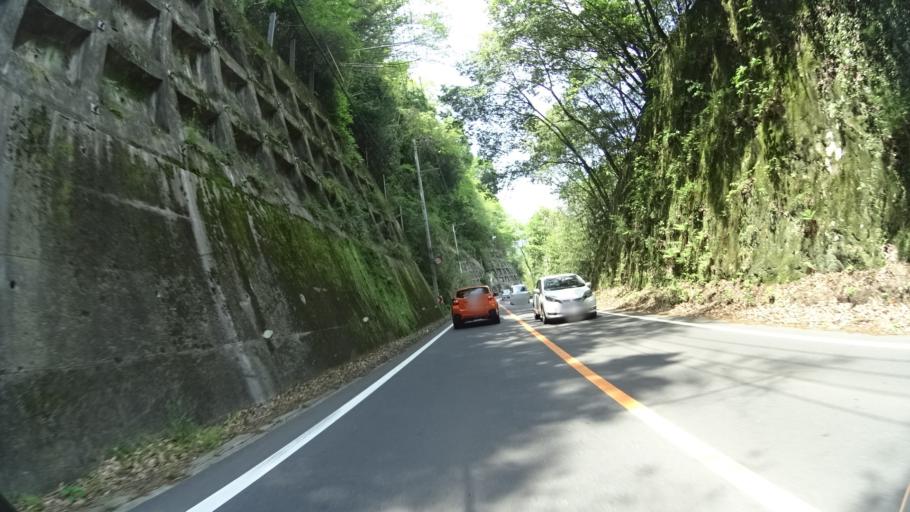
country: JP
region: Ehime
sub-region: Shikoku-chuo Shi
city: Matsuyama
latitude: 33.8884
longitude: 132.8357
